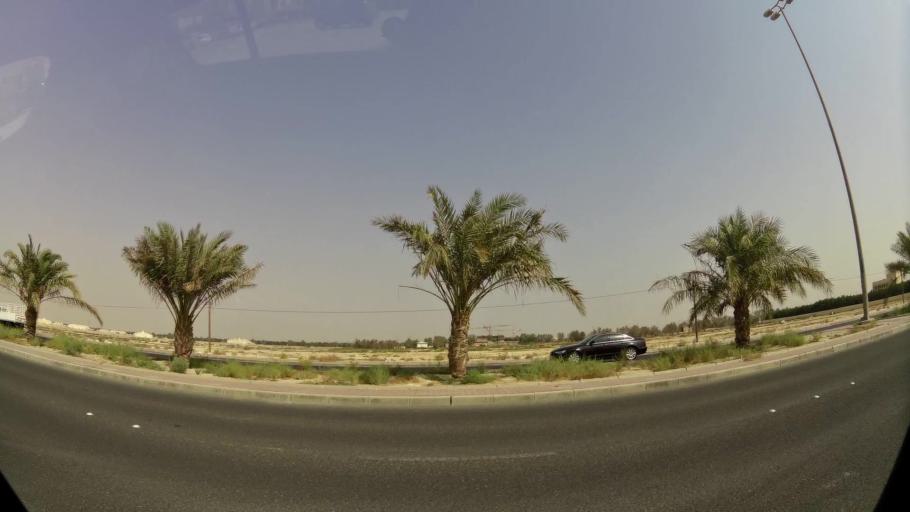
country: KW
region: Muhafazat al Jahra'
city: Al Jahra'
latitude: 29.3246
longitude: 47.7262
